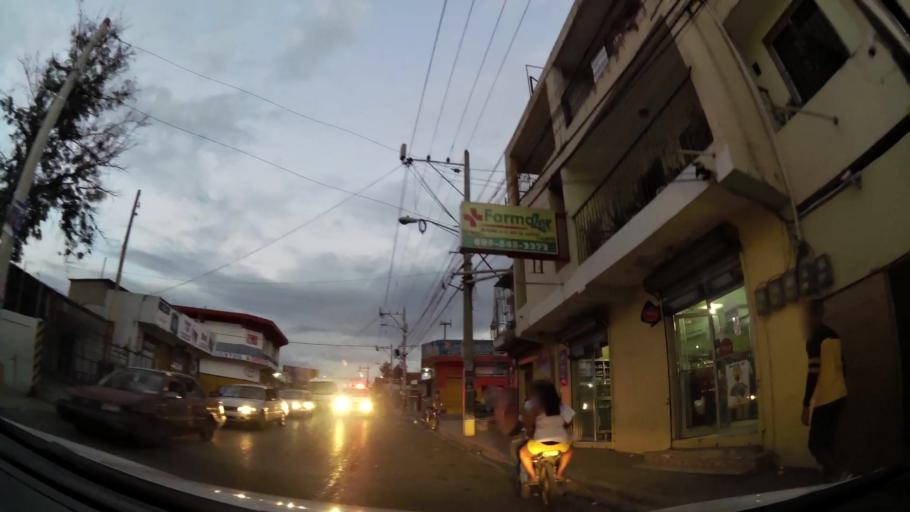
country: DO
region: Santo Domingo
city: Santo Domingo Oeste
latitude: 18.5248
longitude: -70.0286
